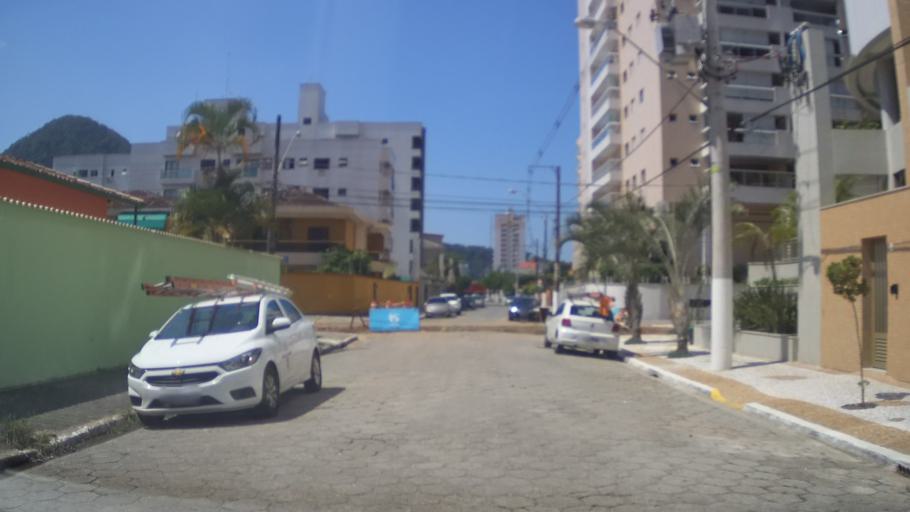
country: BR
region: Sao Paulo
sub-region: Praia Grande
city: Praia Grande
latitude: -24.0066
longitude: -46.4093
